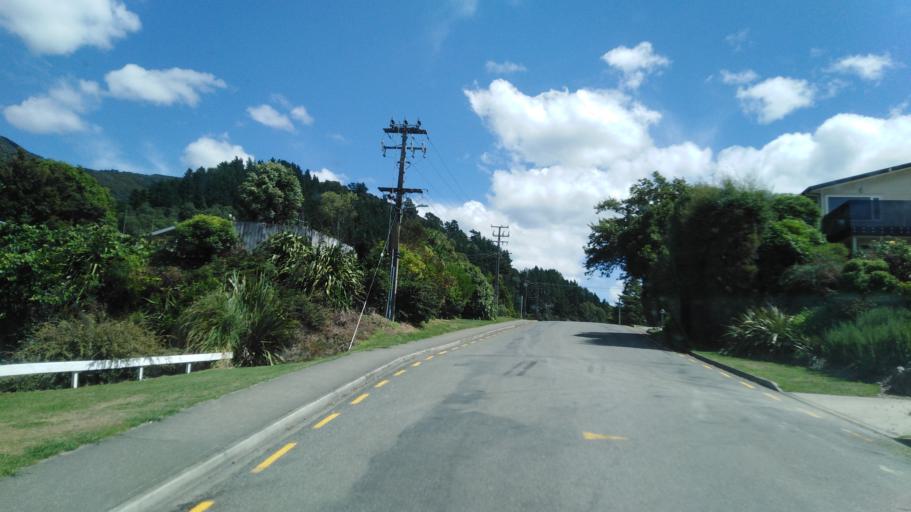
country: NZ
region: Marlborough
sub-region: Marlborough District
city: Picton
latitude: -41.2754
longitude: 173.7687
